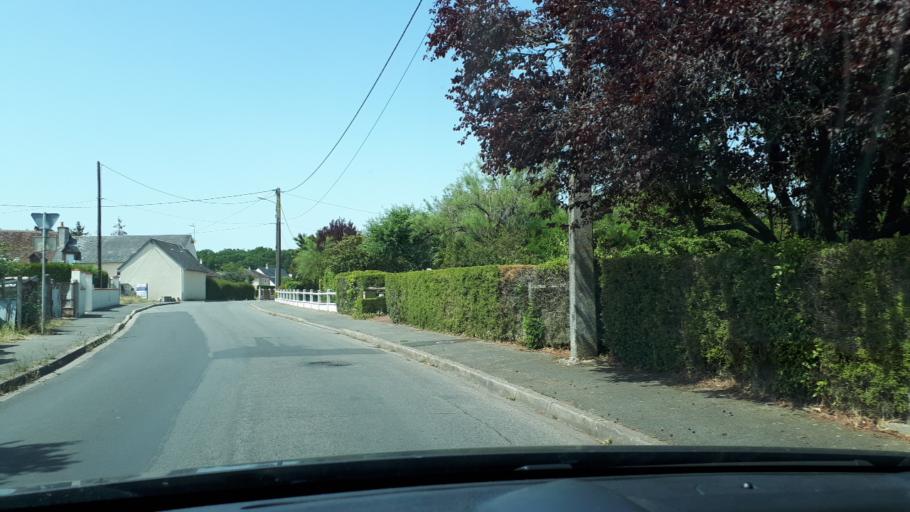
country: FR
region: Centre
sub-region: Departement du Loir-et-Cher
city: Vendome
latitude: 47.8124
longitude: 1.0490
